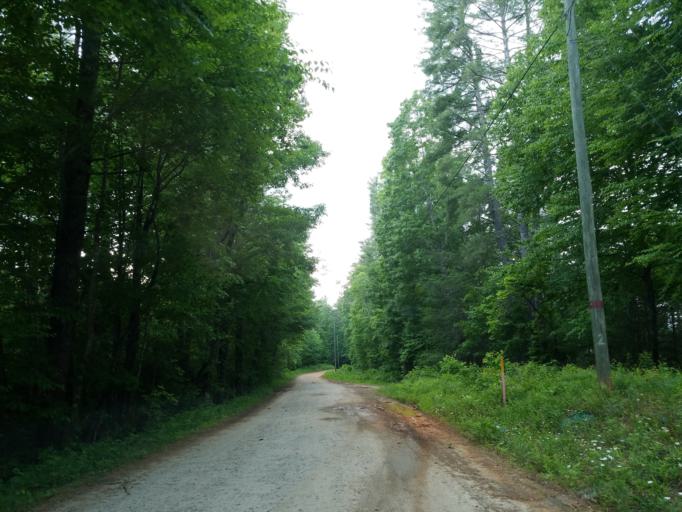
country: US
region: Georgia
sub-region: Lumpkin County
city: Dahlonega
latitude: 34.5987
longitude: -84.0865
